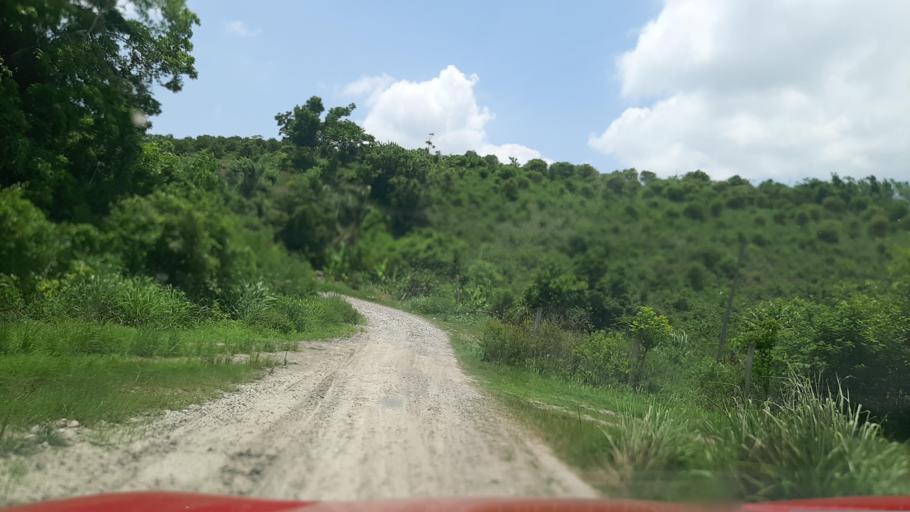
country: MX
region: Veracruz
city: Papantla de Olarte
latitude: 20.4248
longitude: -97.2678
